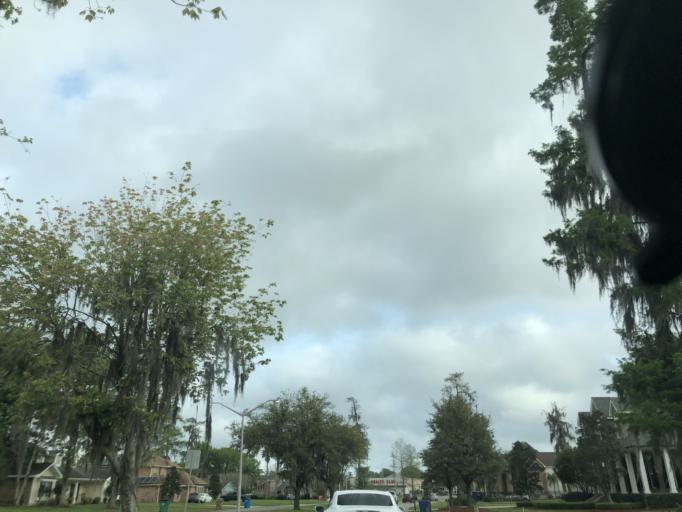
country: US
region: Louisiana
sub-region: Saint Charles Parish
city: New Sarpy
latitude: 29.9837
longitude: -90.3639
